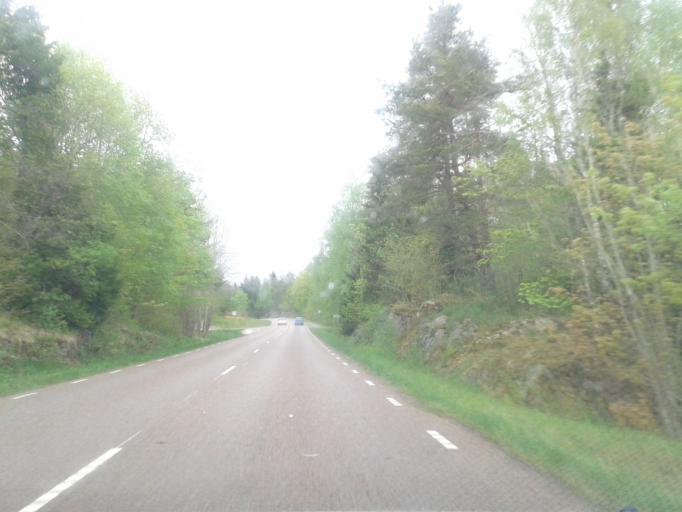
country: SE
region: Vaestra Goetaland
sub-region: Lilla Edets Kommun
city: Lodose
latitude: 58.0734
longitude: 12.1287
